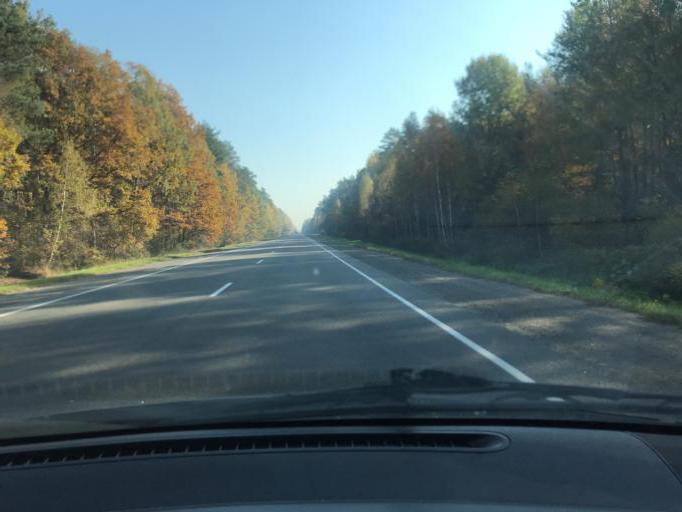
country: BY
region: Brest
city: Horad Luninyets
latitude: 52.2909
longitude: 26.7728
